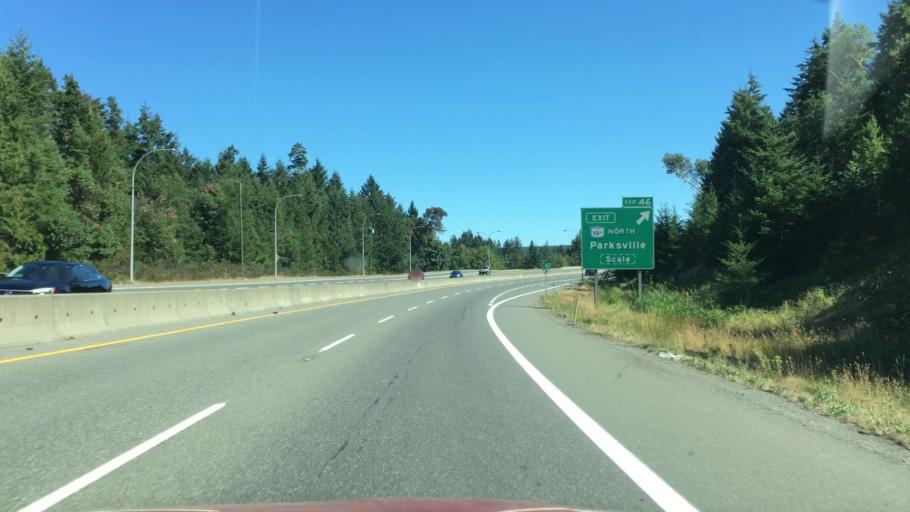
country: CA
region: British Columbia
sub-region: Regional District of Nanaimo
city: Parksville
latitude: 49.3018
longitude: -124.2597
